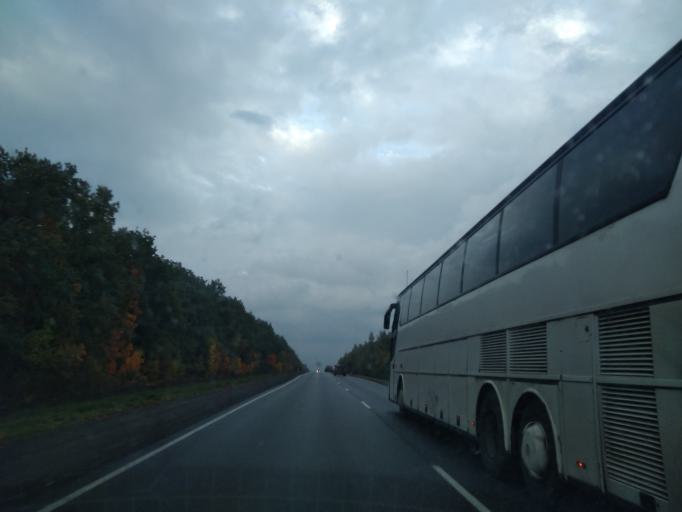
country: RU
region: Lipetsk
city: Borinskoye
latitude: 52.5975
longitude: 39.3003
